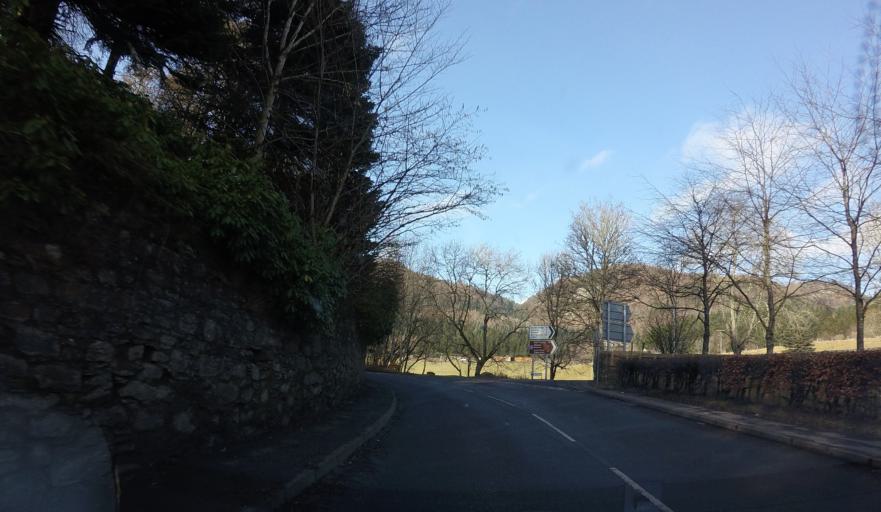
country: GB
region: Scotland
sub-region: Perth and Kinross
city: Bankfoot
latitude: 56.5707
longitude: -3.5911
